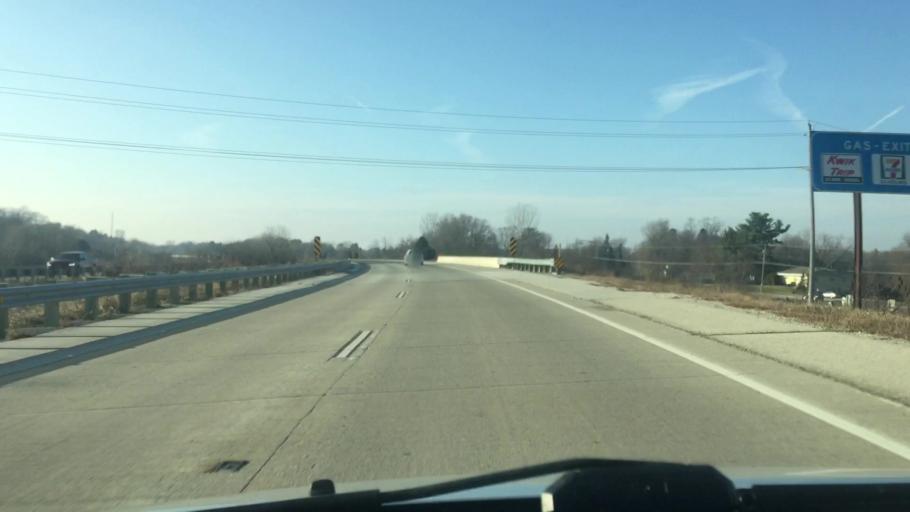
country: US
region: Wisconsin
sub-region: Waukesha County
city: Okauchee Lake
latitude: 43.1075
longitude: -88.4308
